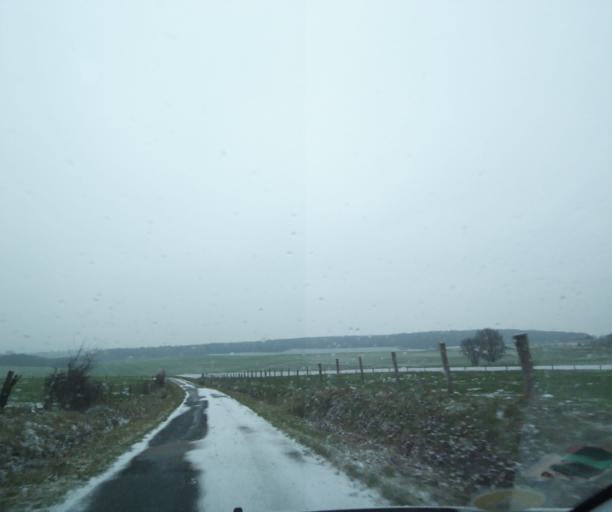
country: FR
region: Champagne-Ardenne
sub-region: Departement de la Haute-Marne
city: Wassy
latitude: 48.4614
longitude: 5.0295
